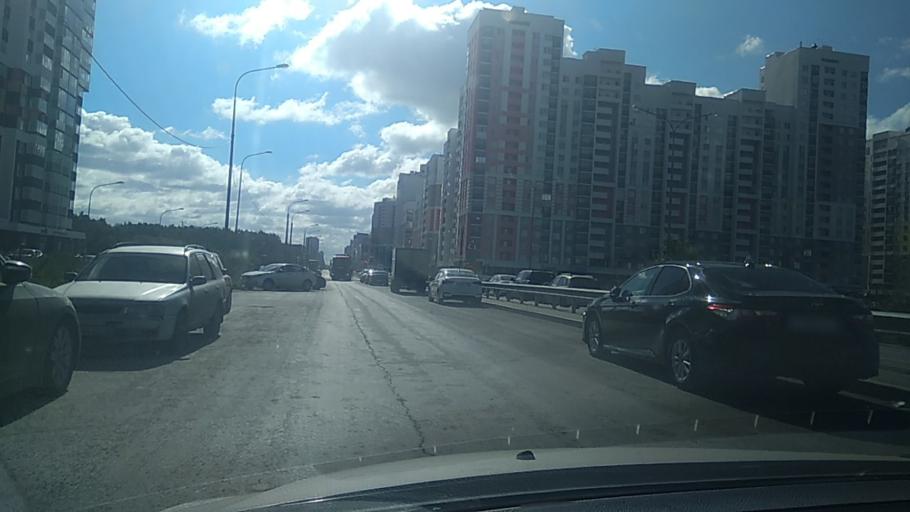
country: RU
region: Sverdlovsk
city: Shirokaya Rechka
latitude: 56.7988
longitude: 60.5115
